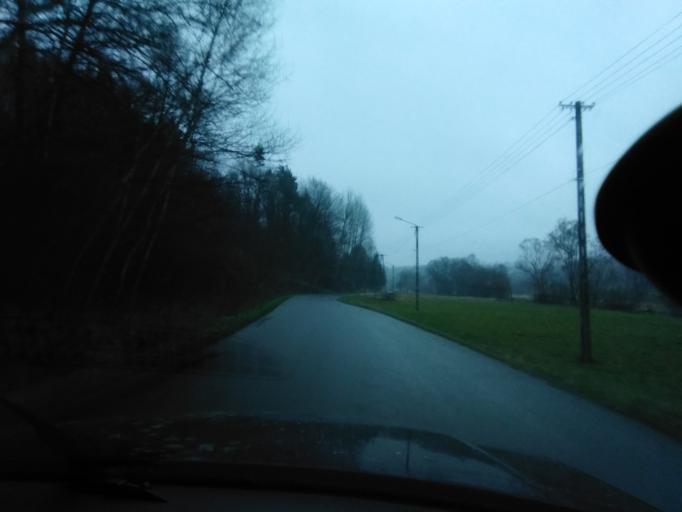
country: PL
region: Subcarpathian Voivodeship
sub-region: Powiat brzozowski
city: Jablonka
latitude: 49.7400
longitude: 22.1336
